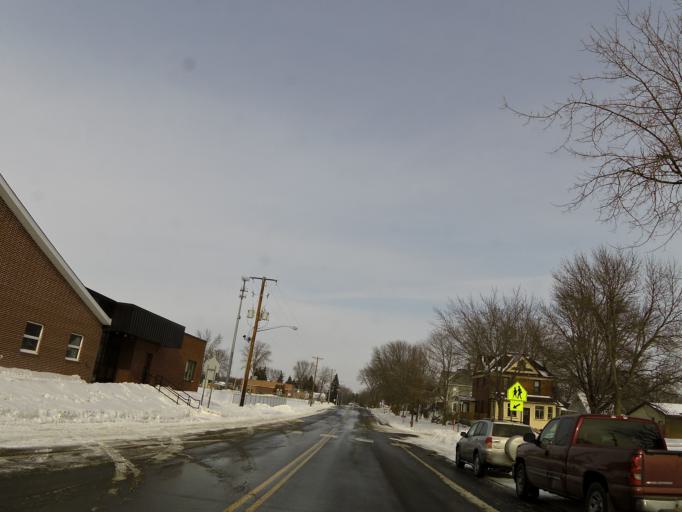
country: US
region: Minnesota
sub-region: Carver County
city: Mayer
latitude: 44.8865
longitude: -93.8894
